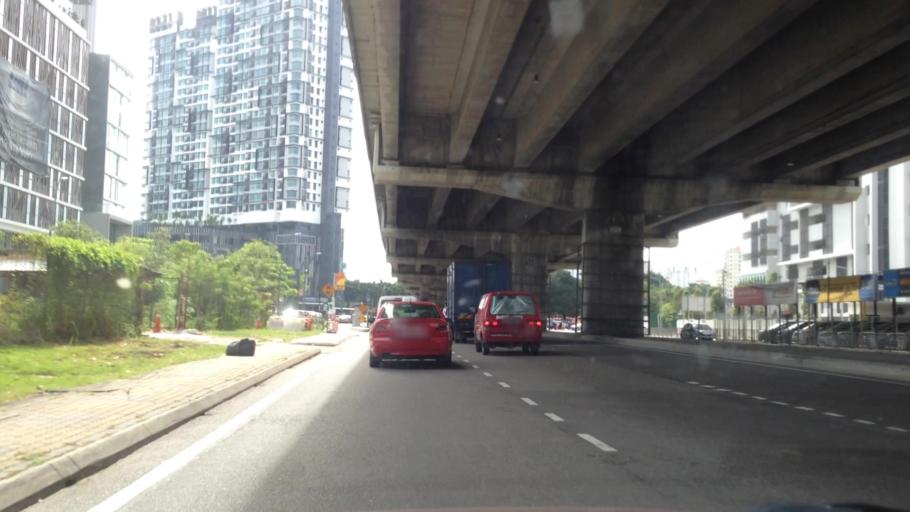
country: MY
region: Selangor
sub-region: Petaling
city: Petaling Jaya
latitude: 3.0832
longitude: 101.6605
